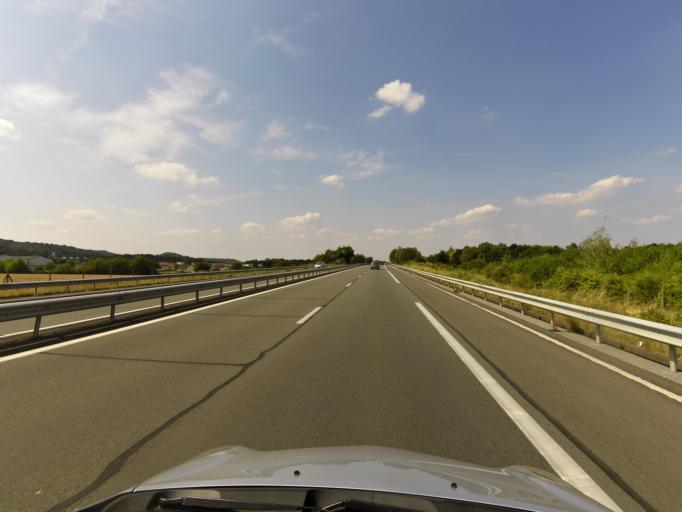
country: FR
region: Picardie
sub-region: Departement de l'Aisne
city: Saint-Erme-Outre-et-Ramecourt
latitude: 49.5285
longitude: 3.8666
